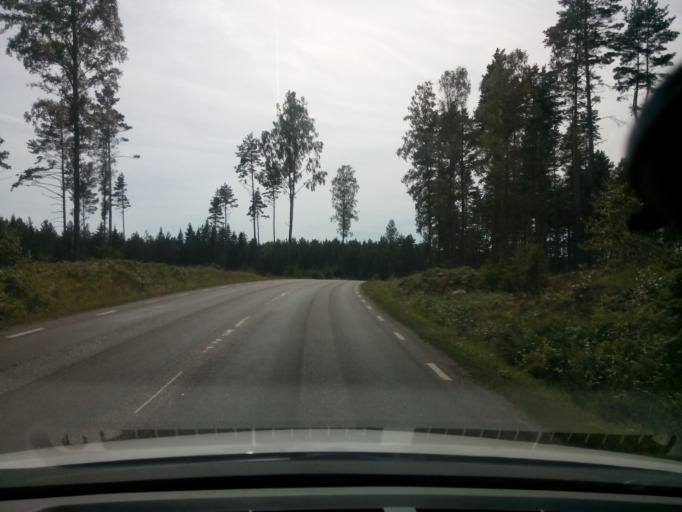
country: SE
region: Soedermanland
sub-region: Oxelosunds Kommun
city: Oxelosund
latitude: 58.7646
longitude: 17.3311
